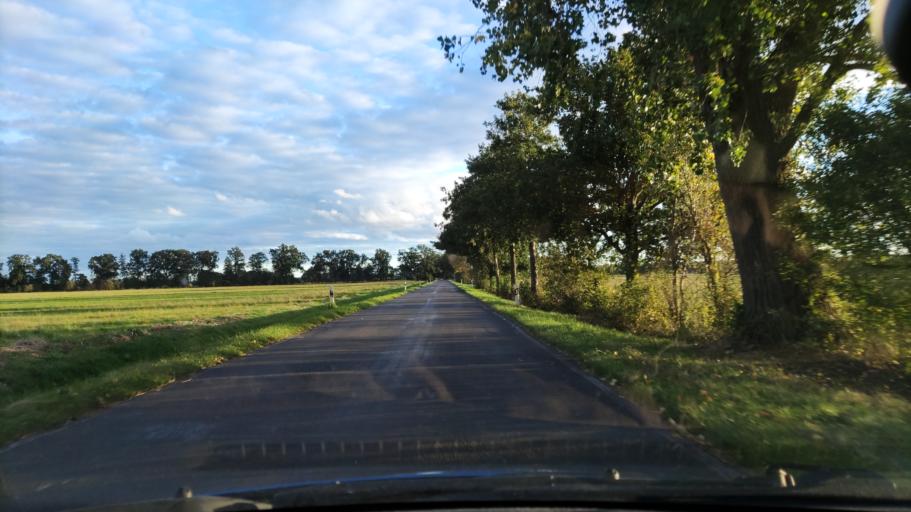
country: DE
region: Lower Saxony
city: Neu Darchau
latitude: 53.3616
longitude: 10.8647
